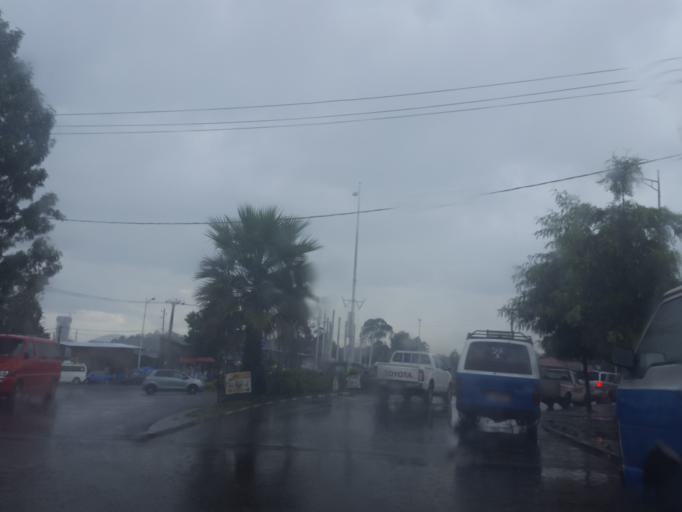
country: ET
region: Adis Abeba
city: Addis Ababa
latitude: 9.0271
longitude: 38.7761
